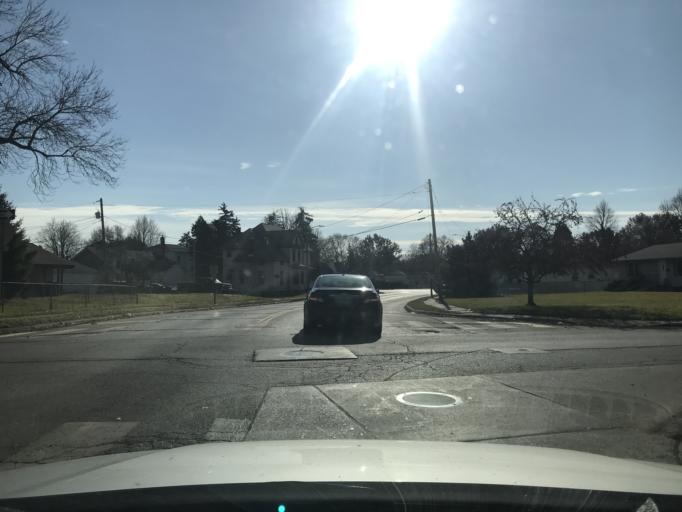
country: US
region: Iowa
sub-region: Scott County
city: Davenport
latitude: 41.5233
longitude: -90.6147
